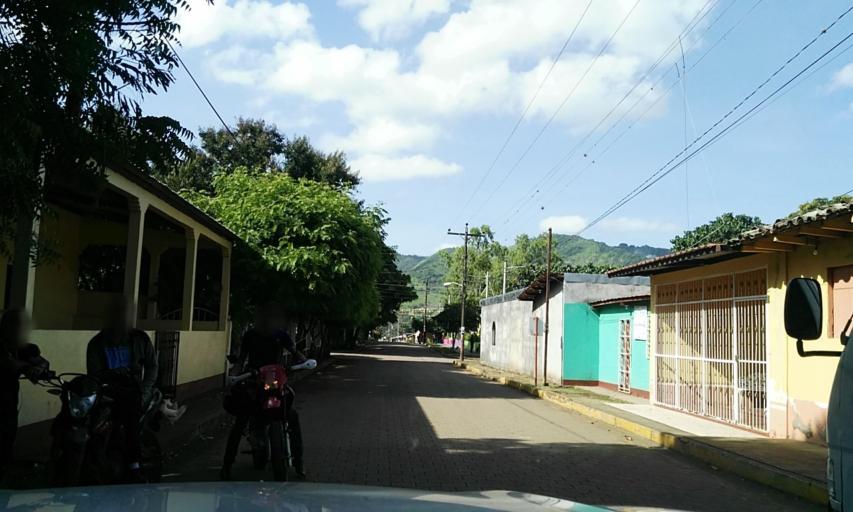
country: NI
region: Matagalpa
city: Terrabona
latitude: 12.7310
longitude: -85.9645
